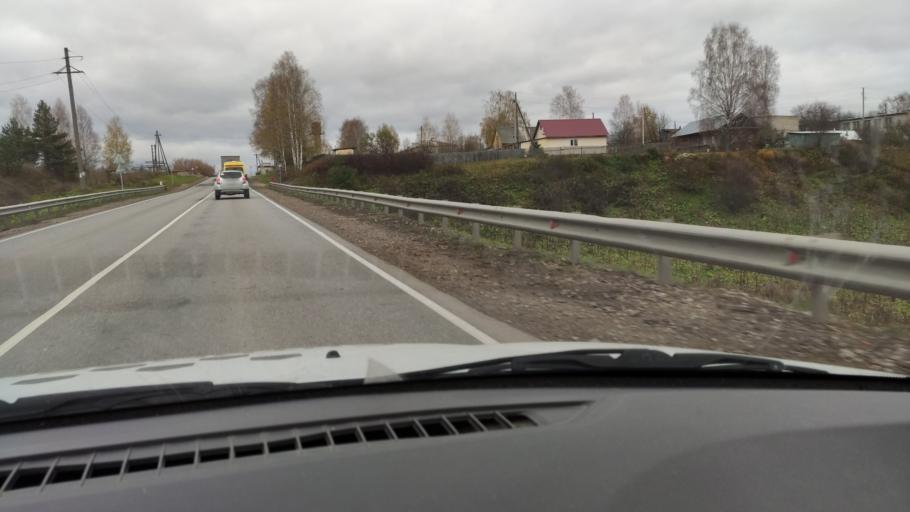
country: RU
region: Kirov
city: Slobodskoy
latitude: 58.7821
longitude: 50.4200
